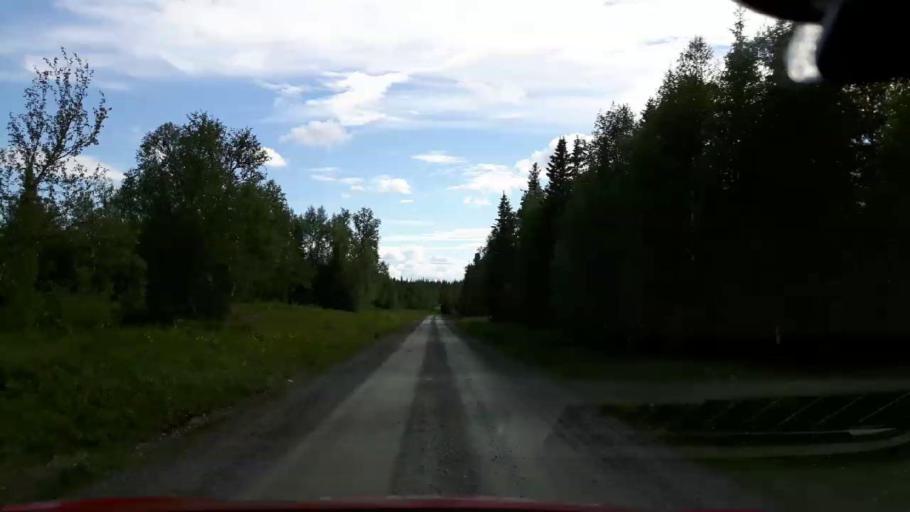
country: SE
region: Jaemtland
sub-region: Krokoms Kommun
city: Valla
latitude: 63.8720
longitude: 14.1216
